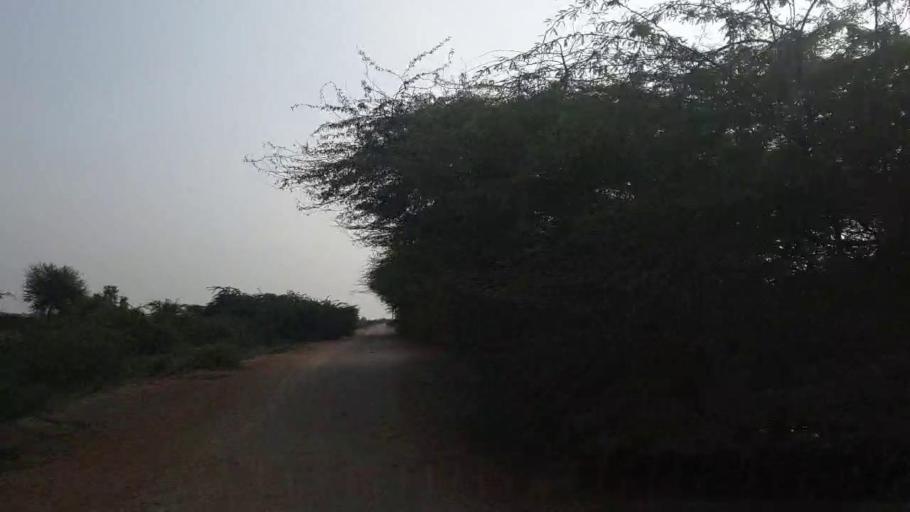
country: PK
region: Sindh
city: Badin
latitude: 24.6342
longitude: 68.6924
